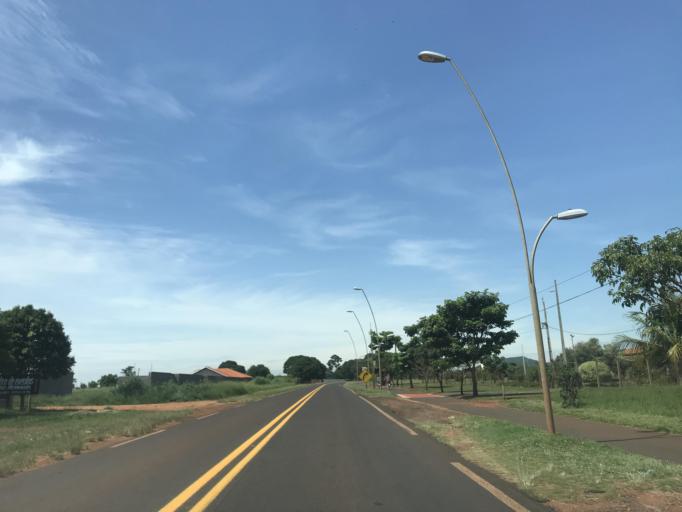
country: BR
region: Parana
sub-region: Terra Rica
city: Terra Rica
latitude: -22.7487
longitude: -52.6252
